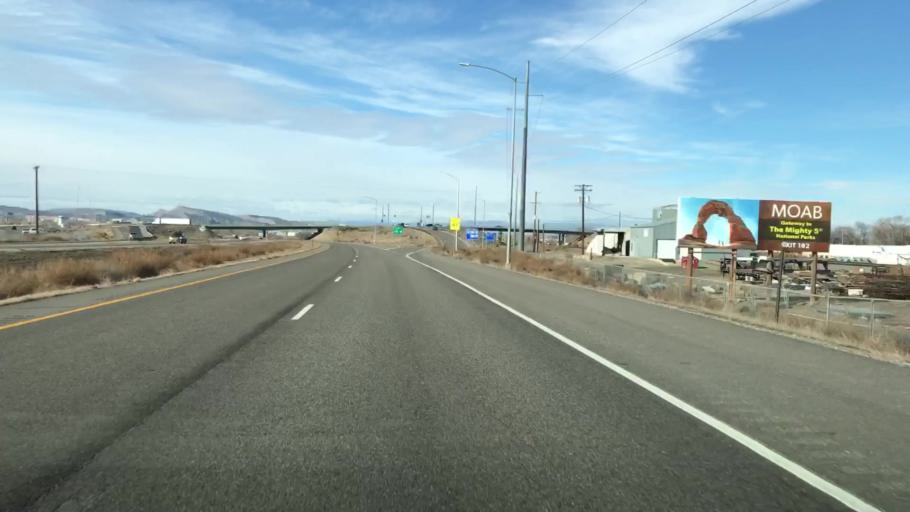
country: US
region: Colorado
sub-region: Mesa County
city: Fruita
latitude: 39.1508
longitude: -108.7328
